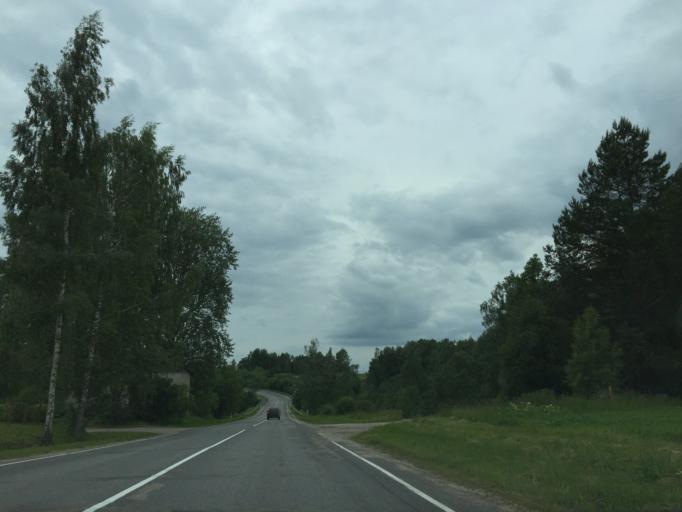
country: LV
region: Apes Novads
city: Ape
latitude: 57.4542
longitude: 26.3527
